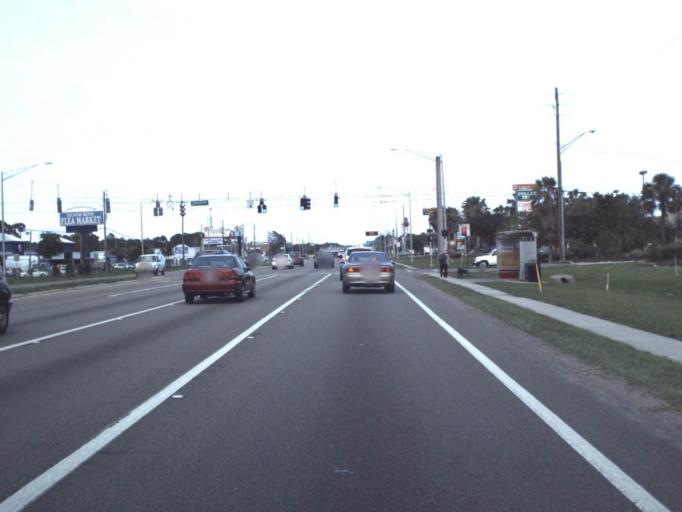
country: US
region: Florida
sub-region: Duval County
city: Jacksonville
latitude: 30.2867
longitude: -81.5344
